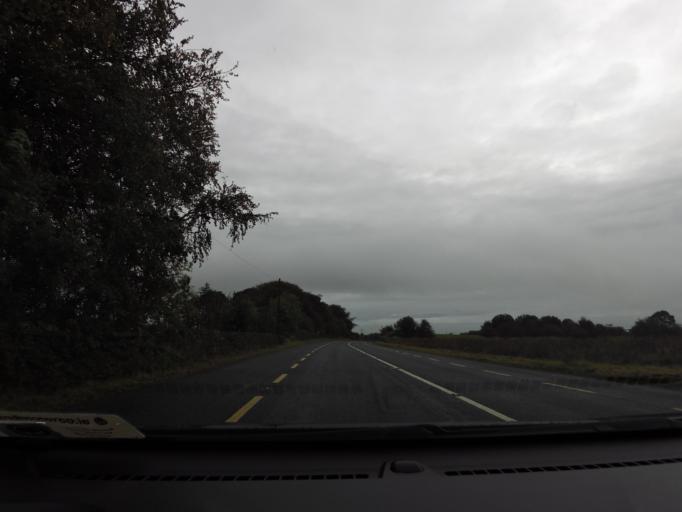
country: IE
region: Connaught
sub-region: County Galway
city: Tuam
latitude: 53.5660
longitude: -8.7919
